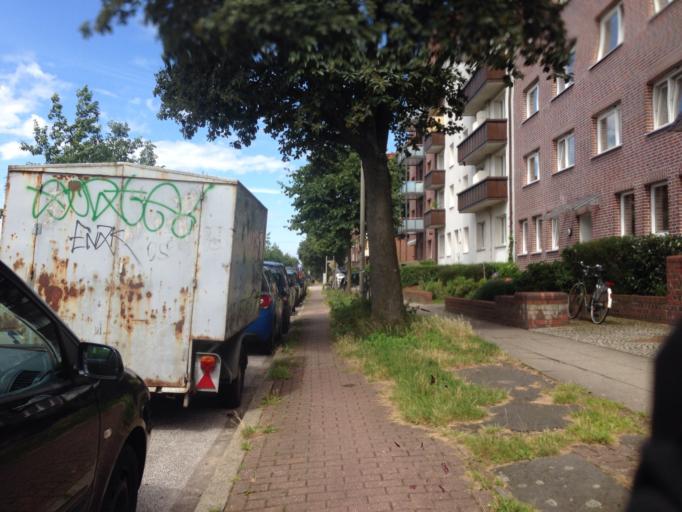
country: DE
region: Hamburg
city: Barmbek-Nord
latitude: 53.5941
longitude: 10.0378
